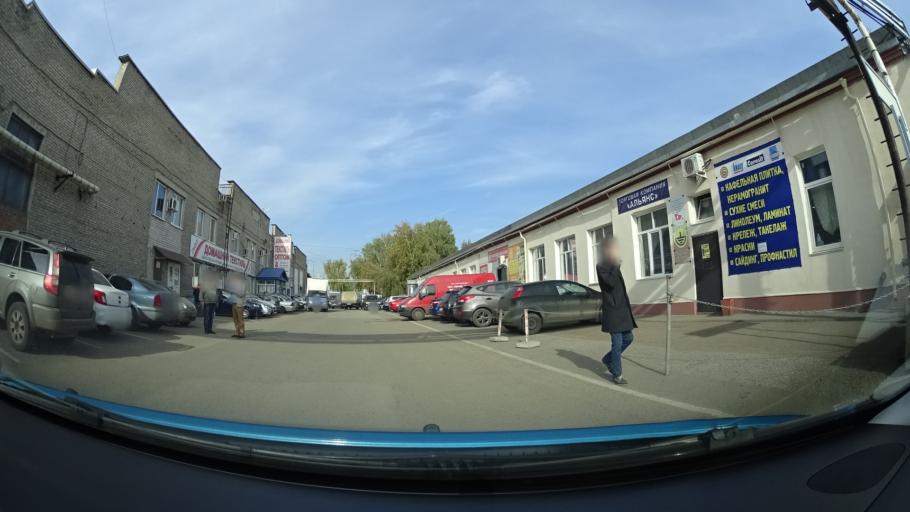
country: RU
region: Bashkortostan
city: Ufa
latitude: 54.7958
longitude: 56.0620
